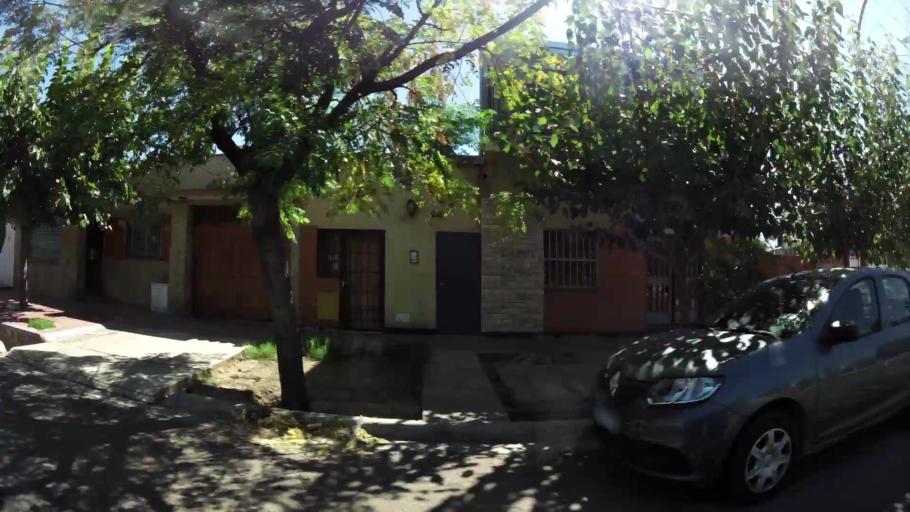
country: AR
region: Mendoza
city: Villa Nueva
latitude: -32.8990
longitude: -68.7788
